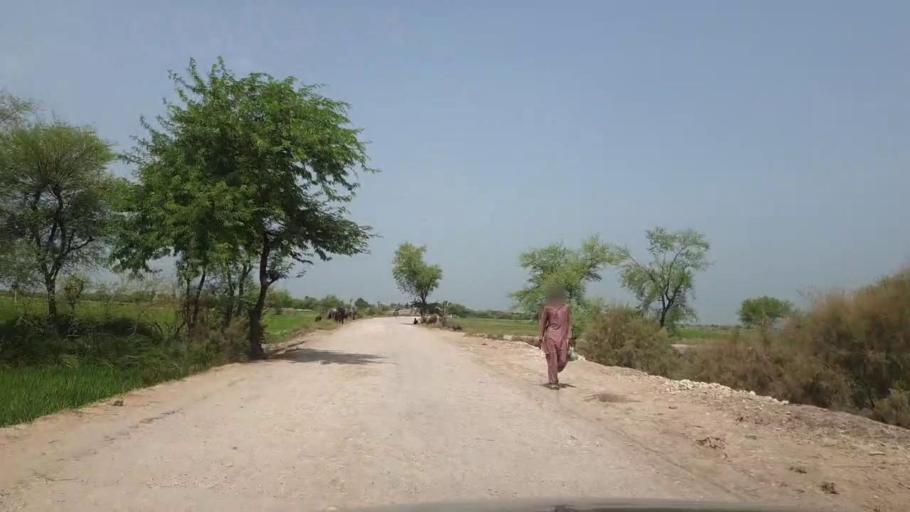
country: PK
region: Sindh
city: Garhi Yasin
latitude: 27.8559
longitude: 68.4206
